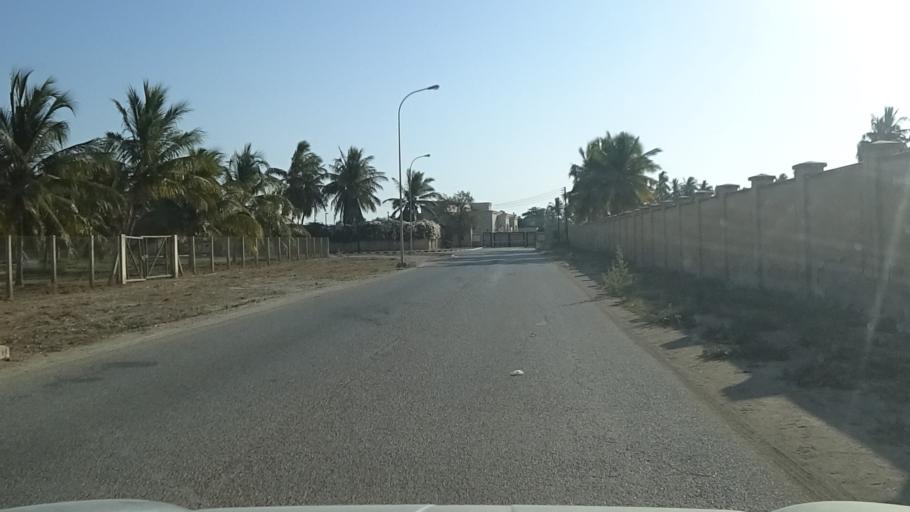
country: OM
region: Zufar
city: Salalah
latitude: 17.0184
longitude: 54.1485
